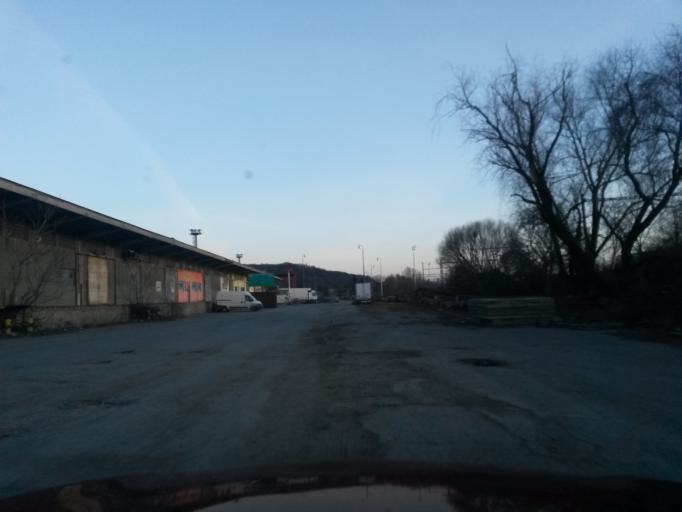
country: SK
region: Kosicky
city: Kosice
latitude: 48.7191
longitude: 21.2725
